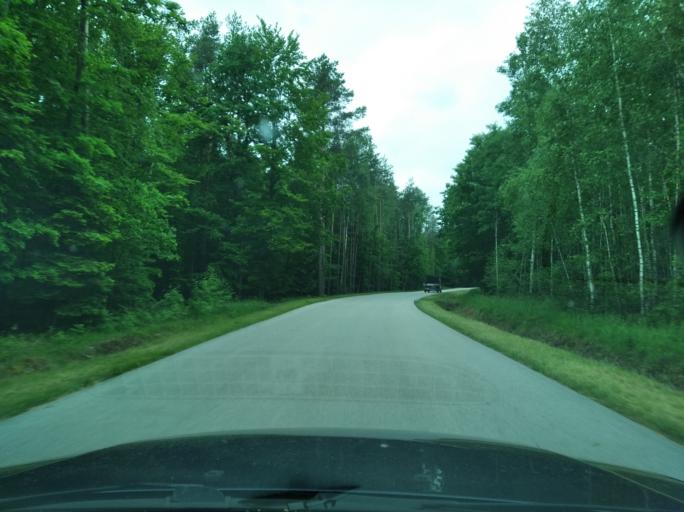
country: PL
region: Subcarpathian Voivodeship
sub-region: Powiat kolbuszowski
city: Niwiska
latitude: 50.2052
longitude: 21.6440
